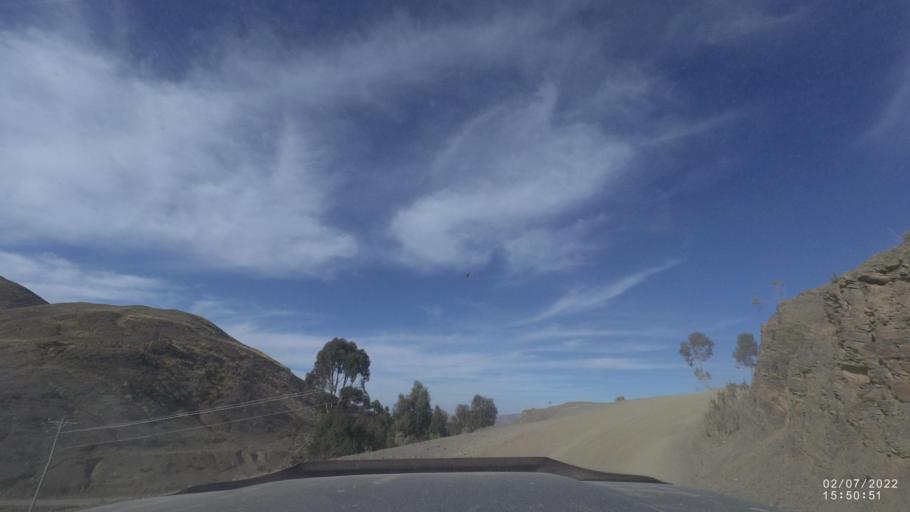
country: BO
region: Cochabamba
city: Irpa Irpa
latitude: -17.9039
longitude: -66.4138
